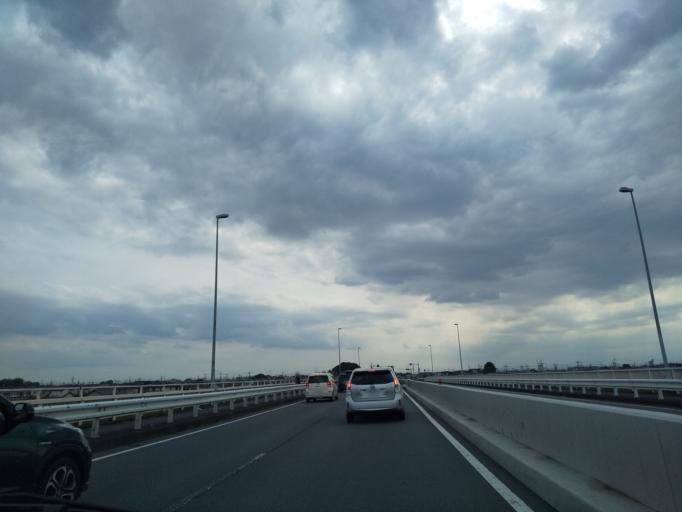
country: JP
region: Chiba
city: Noda
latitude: 35.9910
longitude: 139.8180
